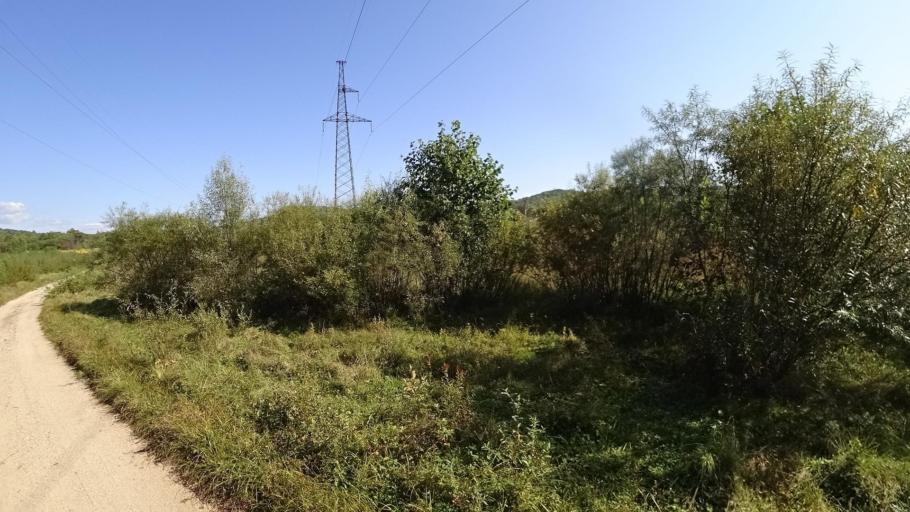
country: RU
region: Jewish Autonomous Oblast
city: Bira
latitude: 49.0003
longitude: 132.4769
